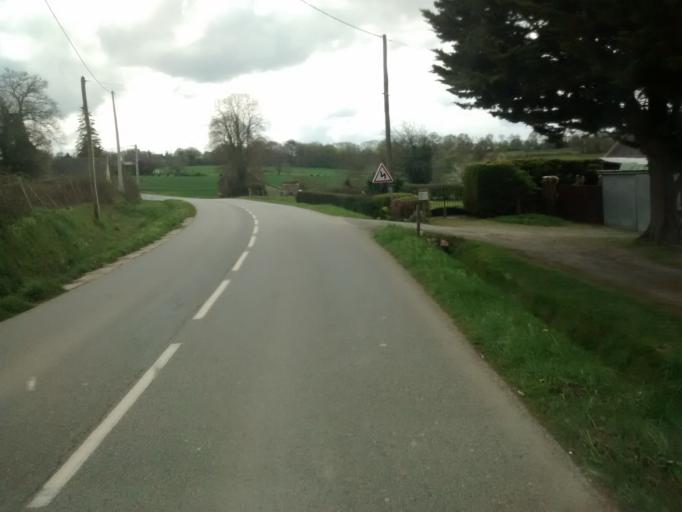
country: FR
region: Brittany
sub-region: Departement du Morbihan
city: Caro
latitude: 47.8898
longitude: -2.3629
